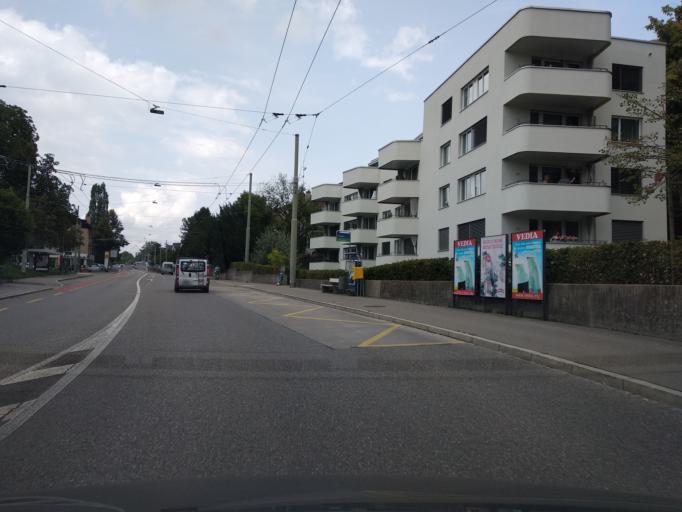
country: CH
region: Zurich
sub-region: Bezirk Winterthur
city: Veltheim
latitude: 47.5132
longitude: 8.7220
